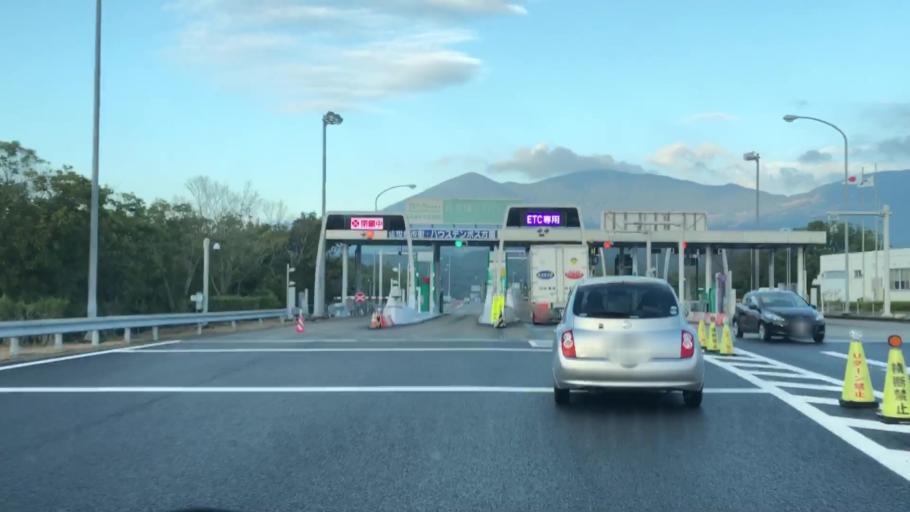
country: JP
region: Saga Prefecture
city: Imaricho-ko
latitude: 33.1696
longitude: 129.8490
